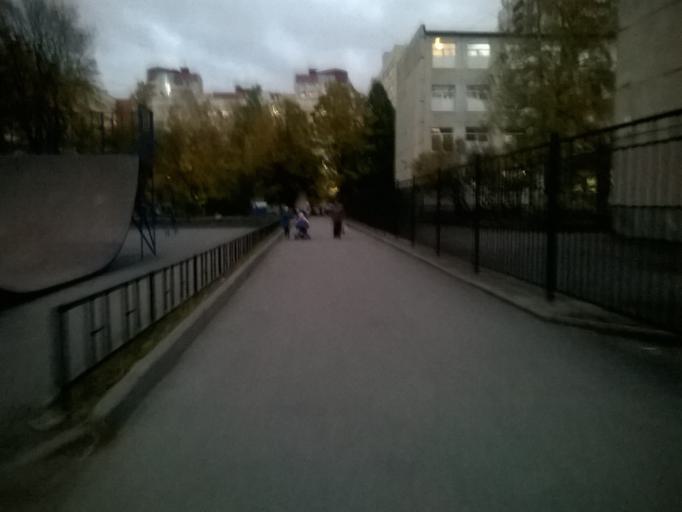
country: RU
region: St.-Petersburg
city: Ozerki
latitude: 60.0339
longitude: 30.3251
